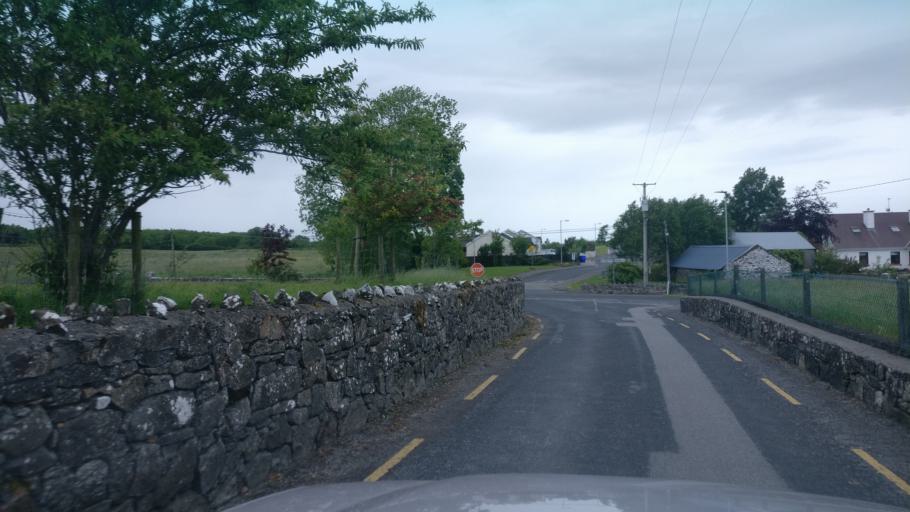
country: IE
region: Connaught
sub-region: County Galway
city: Portumna
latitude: 53.1043
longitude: -8.3942
